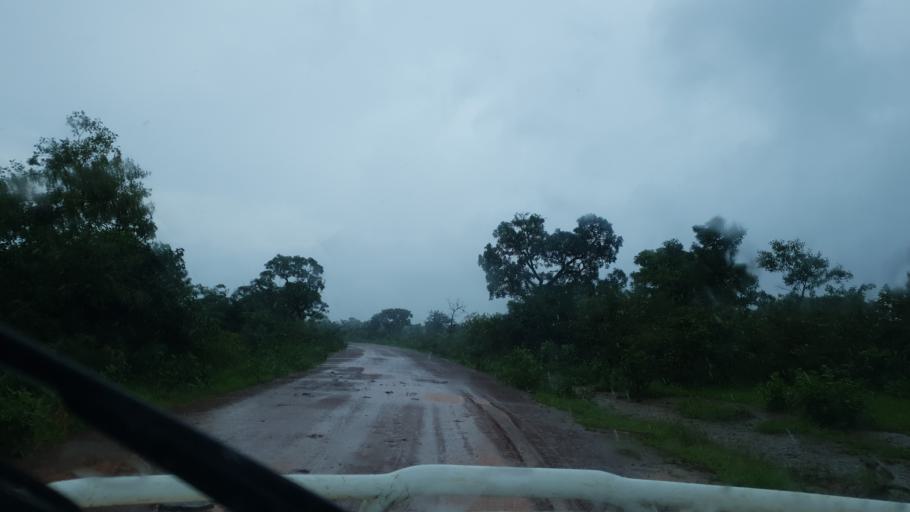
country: ML
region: Sikasso
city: Kolondieba
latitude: 11.6054
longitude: -6.6748
